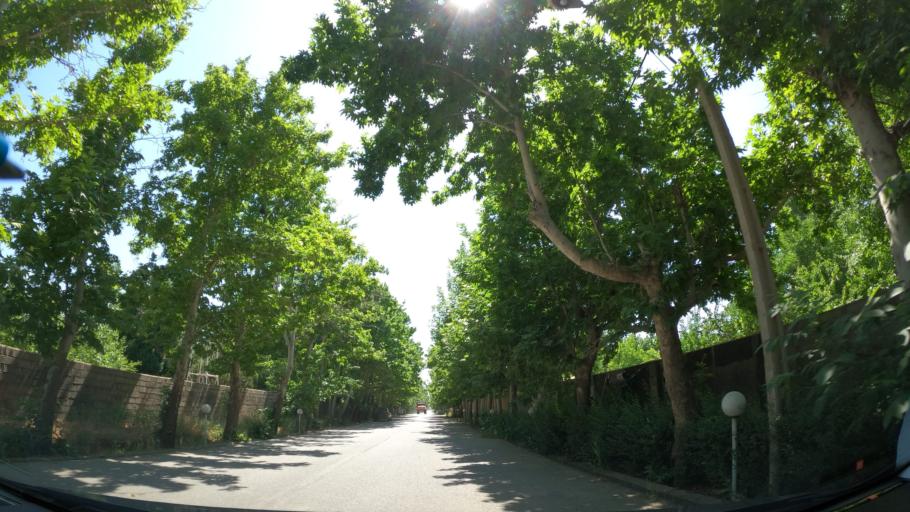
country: IR
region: Alborz
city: Hashtgerd
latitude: 35.9163
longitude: 50.7282
